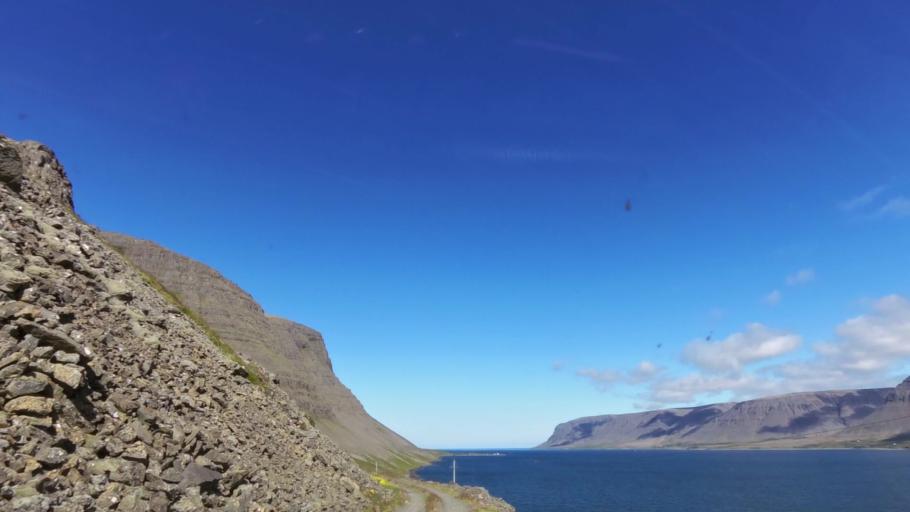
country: IS
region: West
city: Olafsvik
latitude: 65.6241
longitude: -23.8877
